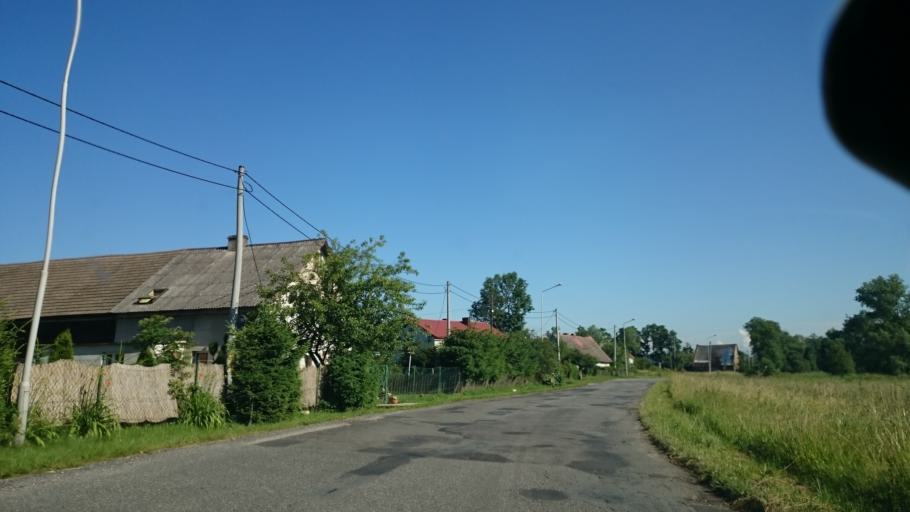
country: PL
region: Lower Silesian Voivodeship
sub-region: Powiat klodzki
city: Bystrzyca Klodzka
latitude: 50.2707
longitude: 16.6403
